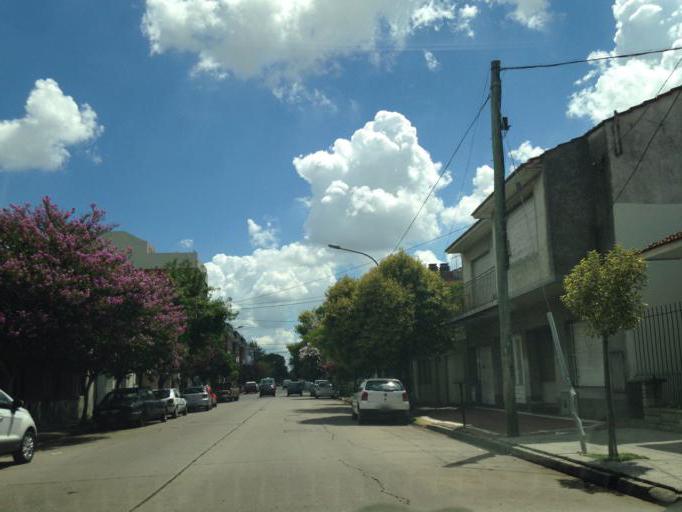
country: AR
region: Buenos Aires
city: Mar del Plata
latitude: -38.0091
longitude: -57.5590
